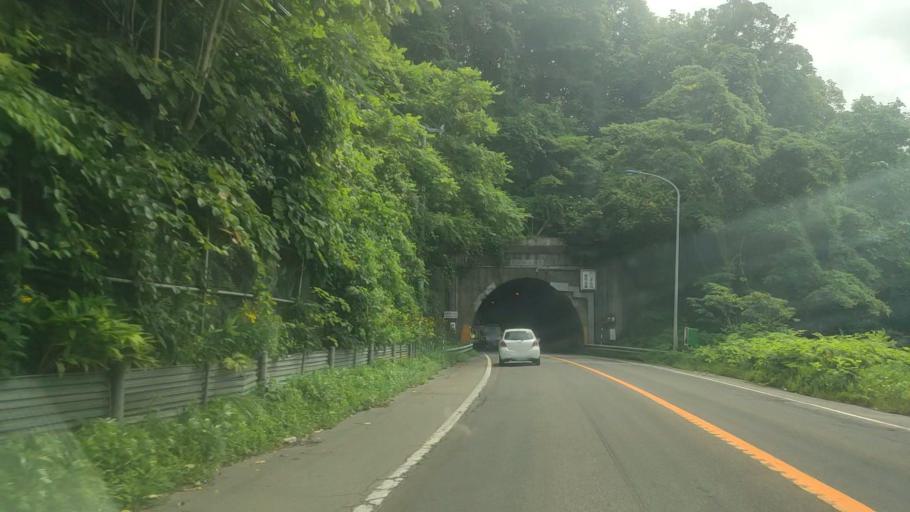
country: JP
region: Hokkaido
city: Niseko Town
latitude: 42.5897
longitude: 140.6766
